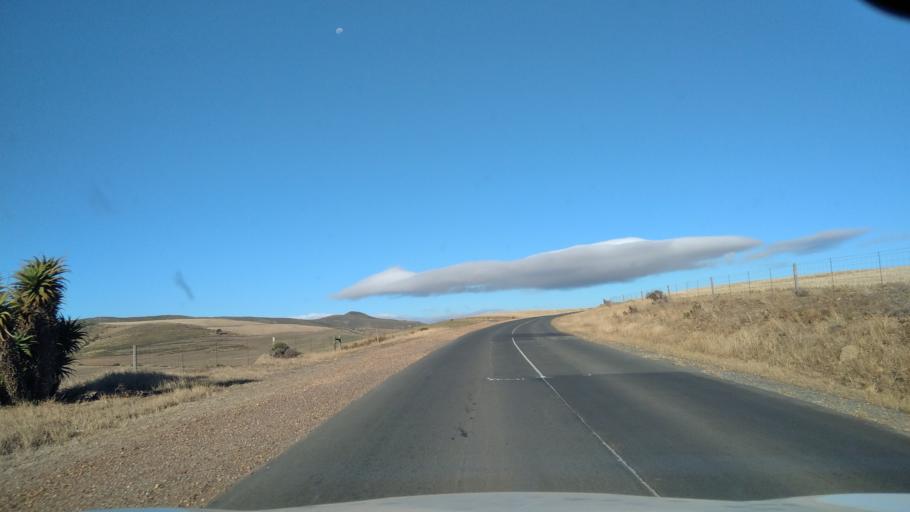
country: ZA
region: Western Cape
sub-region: Overberg District Municipality
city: Caledon
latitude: -34.1670
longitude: 19.2931
